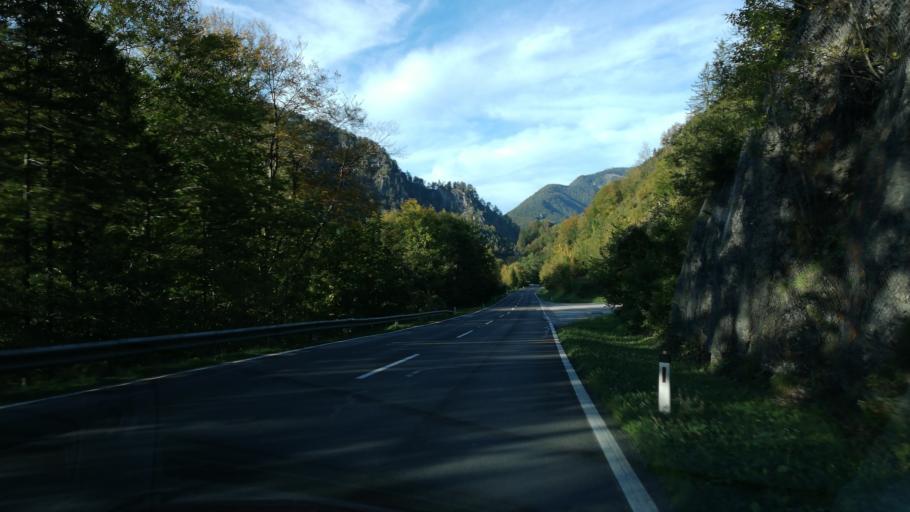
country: AT
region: Styria
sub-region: Politischer Bezirk Liezen
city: Altenmarkt bei Sankt Gallen
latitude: 47.7561
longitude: 14.6456
